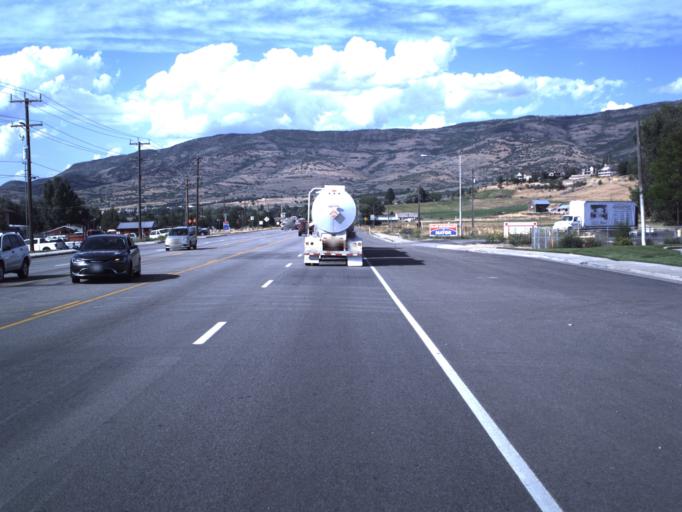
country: US
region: Utah
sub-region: Wasatch County
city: Heber
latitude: 40.5152
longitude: -111.4130
